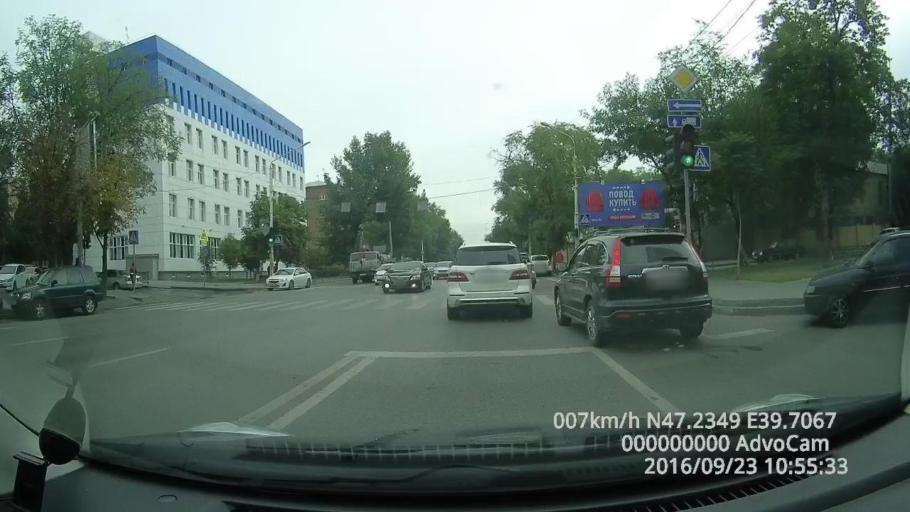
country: RU
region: Rostov
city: Rostov-na-Donu
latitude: 47.2349
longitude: 39.7069
